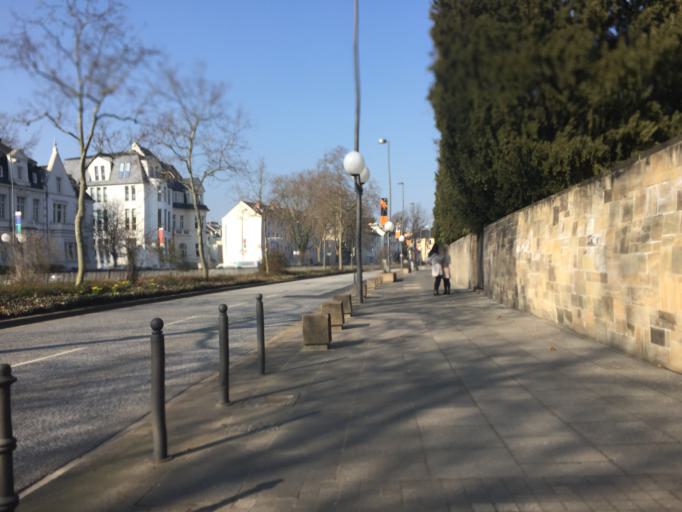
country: DE
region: North Rhine-Westphalia
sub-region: Regierungsbezirk Koln
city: Bonn
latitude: 50.7195
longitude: 7.1173
